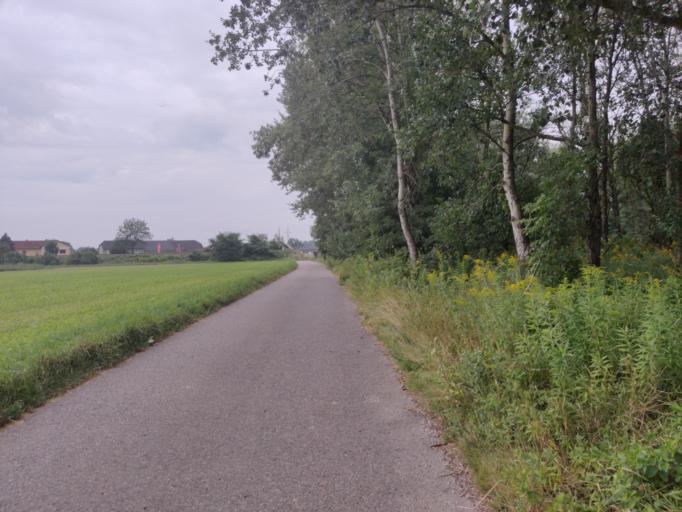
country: AT
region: Lower Austria
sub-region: Politischer Bezirk Amstetten
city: Ennsdorf
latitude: 48.2314
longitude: 14.5318
